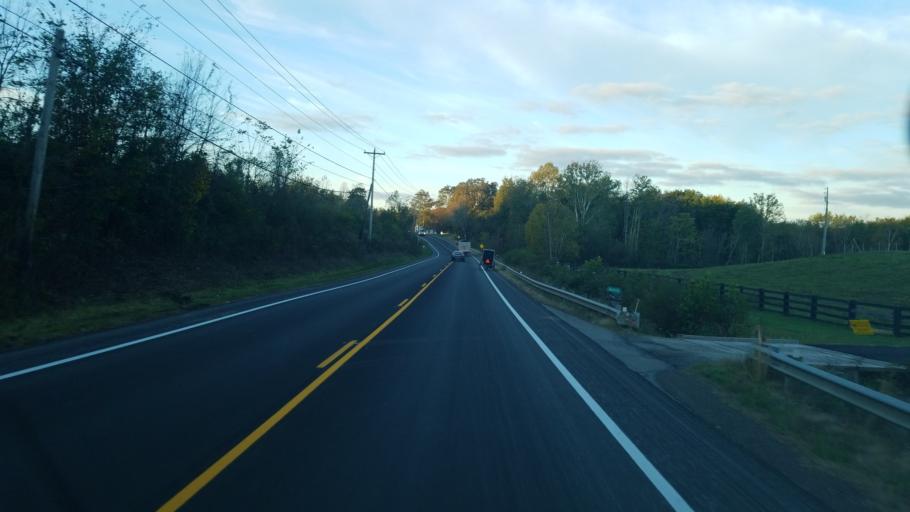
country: US
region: Ohio
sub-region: Vinton County
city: McArthur
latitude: 39.1960
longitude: -82.4993
